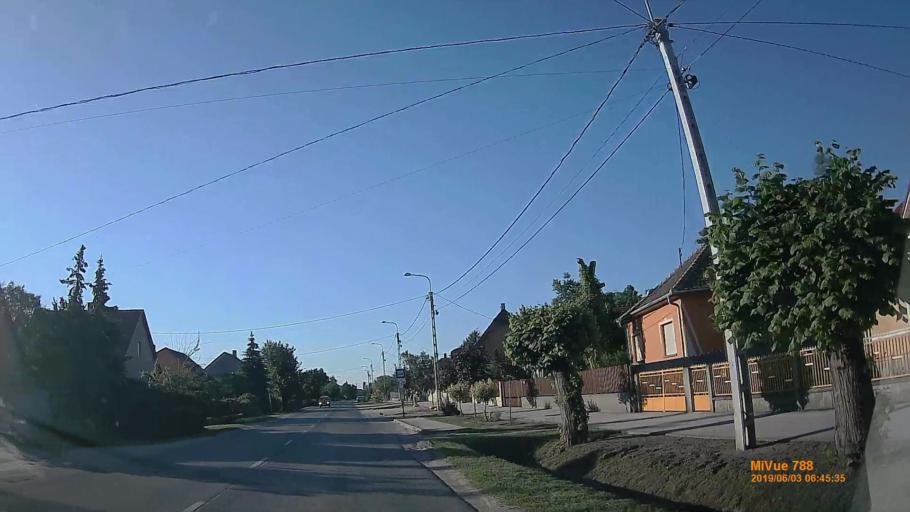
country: HU
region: Pest
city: Bugyi
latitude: 47.2367
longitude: 19.1375
